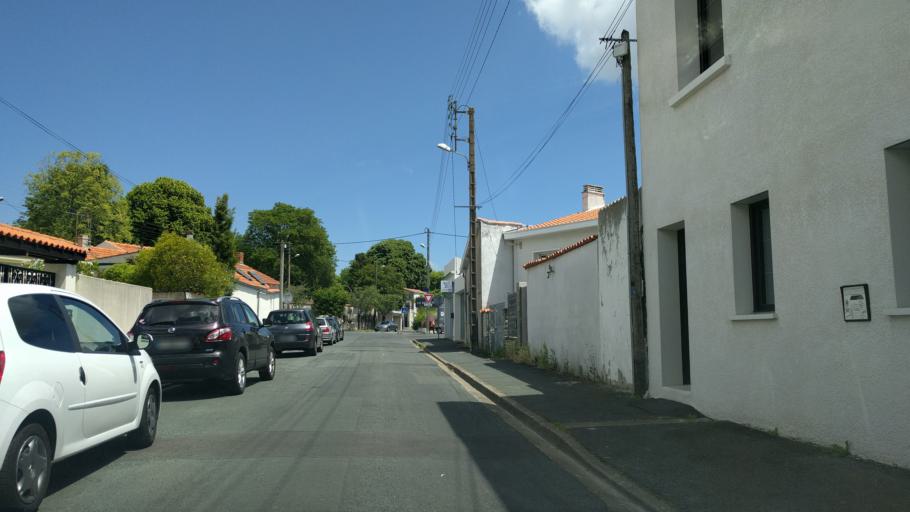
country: FR
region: Poitou-Charentes
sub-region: Departement de la Charente-Maritime
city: La Rochelle
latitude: 46.1626
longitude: -1.1365
